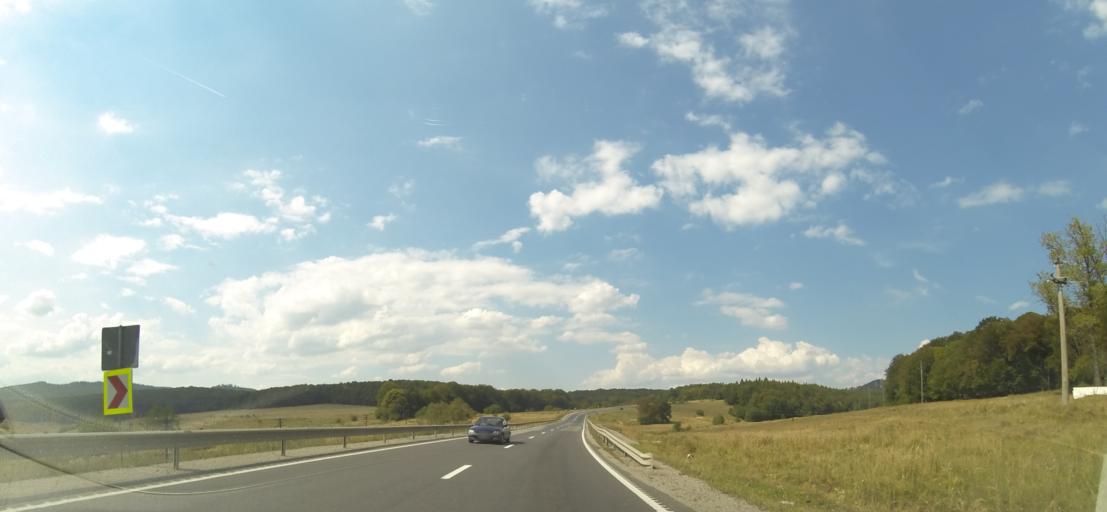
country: RO
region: Brasov
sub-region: Comuna Sinca Noua
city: Sinca Noua
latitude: 45.7451
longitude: 25.2919
